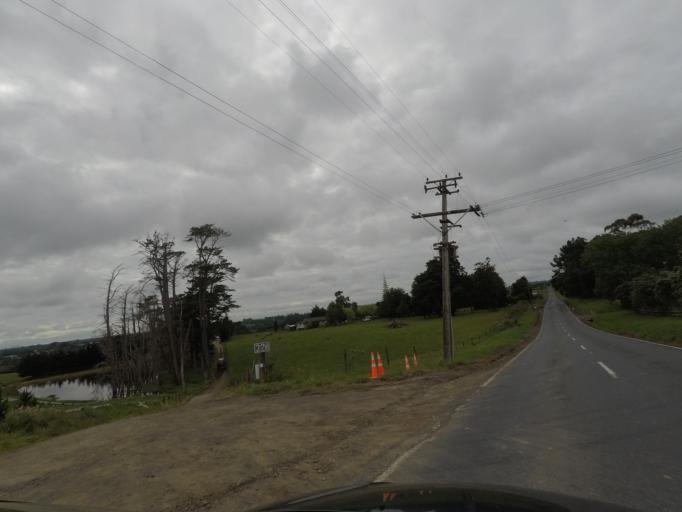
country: NZ
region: Auckland
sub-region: Auckland
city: Rosebank
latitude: -36.8039
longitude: 174.5745
